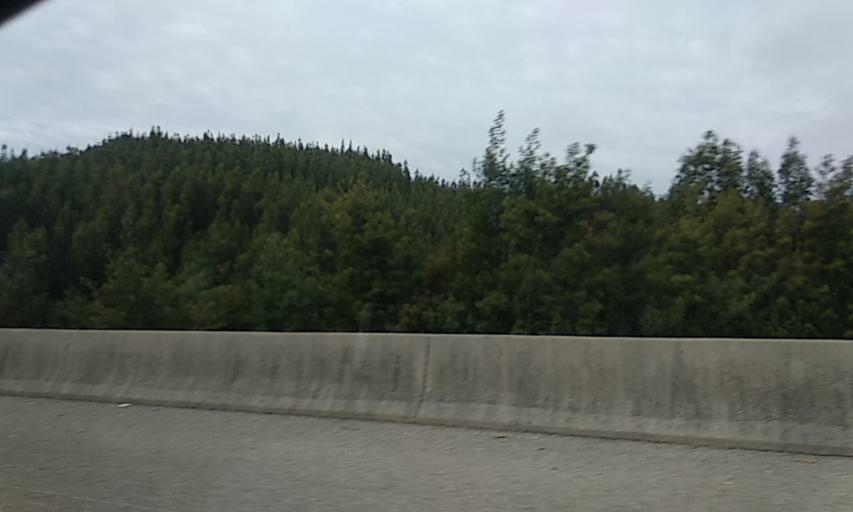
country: PT
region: Porto
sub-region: Trofa
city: Bougado
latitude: 41.3115
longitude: -8.5255
